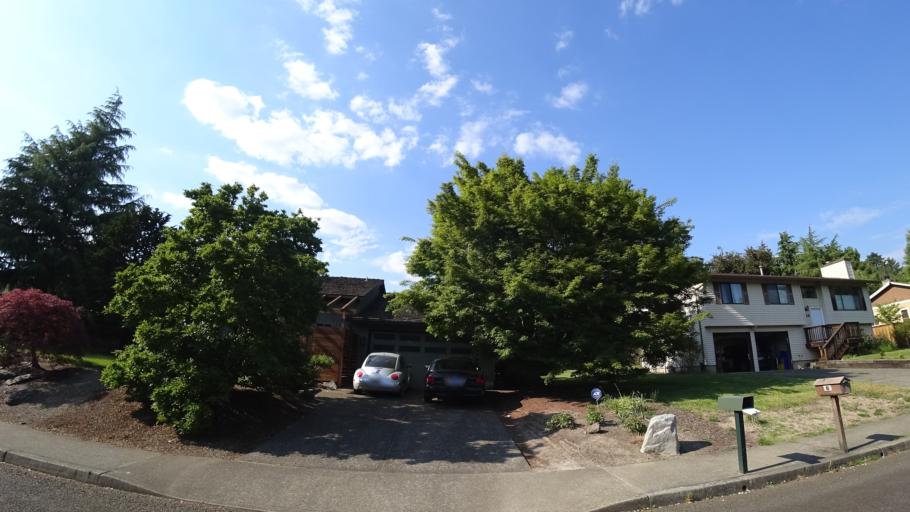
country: US
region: Oregon
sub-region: Washington County
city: Garden Home-Whitford
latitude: 45.4624
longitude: -122.7419
